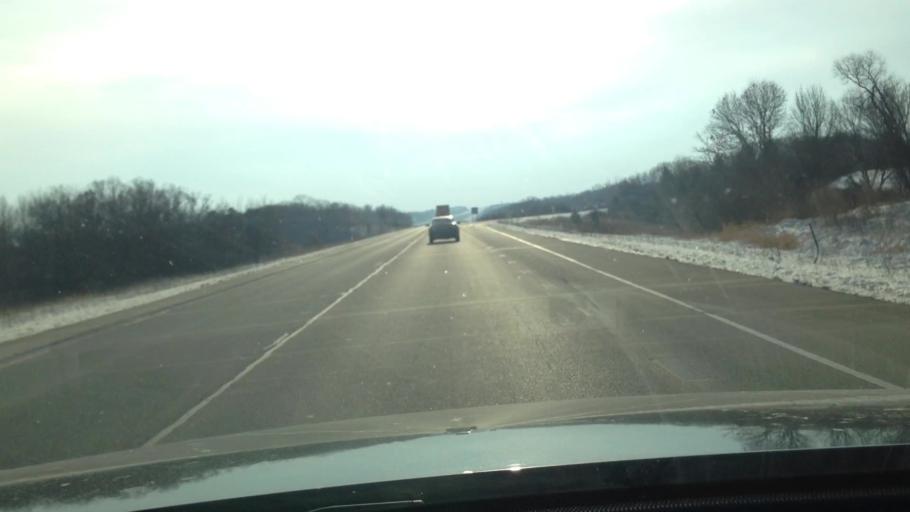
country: US
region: Wisconsin
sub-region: Walworth County
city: East Troy
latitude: 42.7378
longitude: -88.4562
